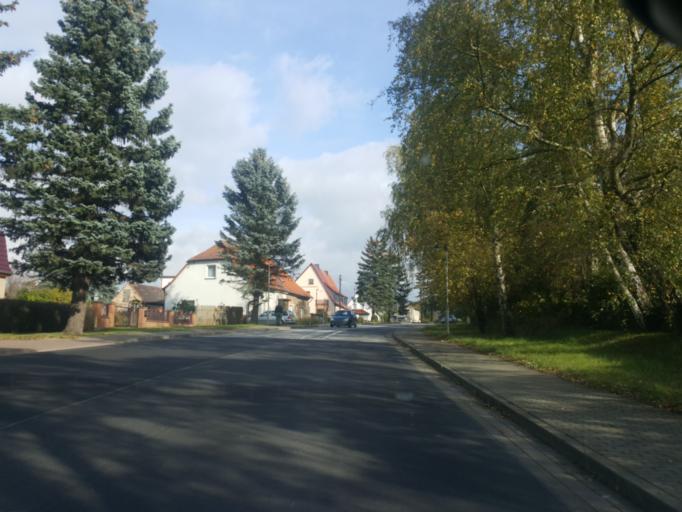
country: DE
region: Saxony-Anhalt
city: Blankenheim
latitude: 51.5174
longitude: 11.4274
